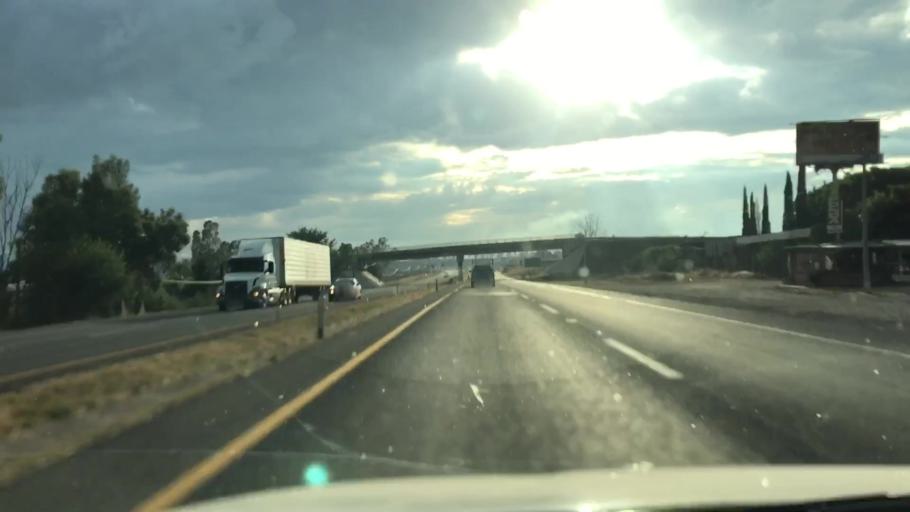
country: MX
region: Guanajuato
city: Penjamo
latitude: 20.3971
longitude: -101.7545
